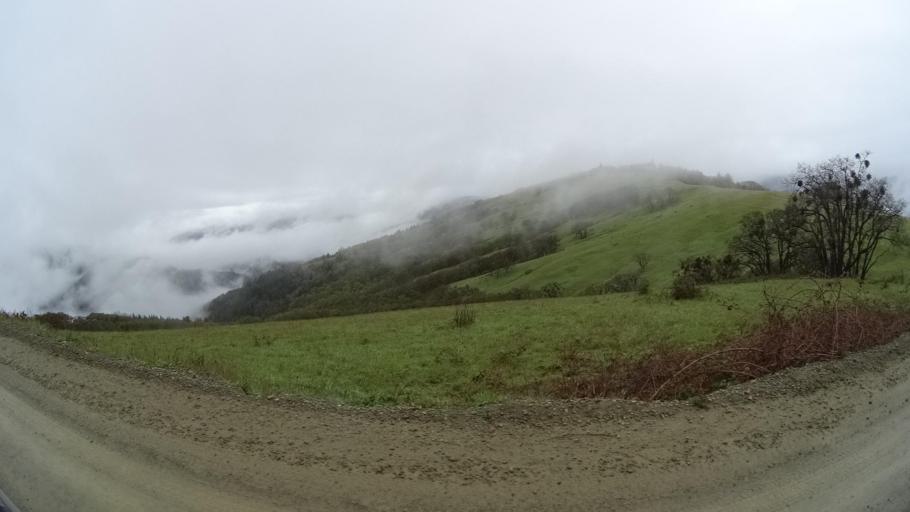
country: US
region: California
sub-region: Humboldt County
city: Westhaven-Moonstone
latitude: 41.1471
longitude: -123.8909
